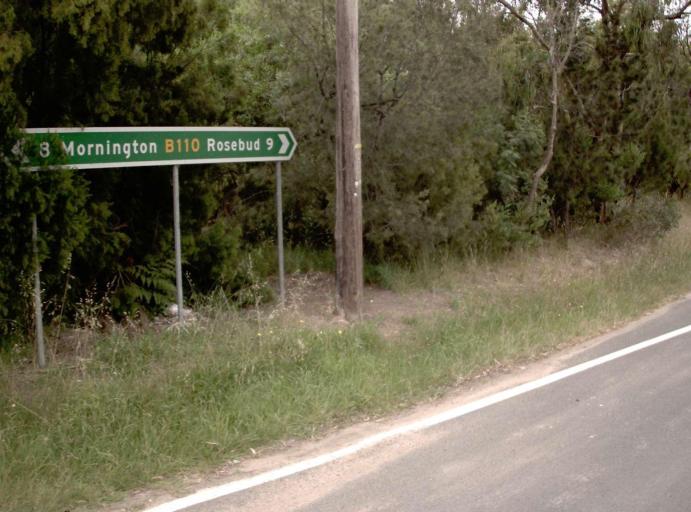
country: AU
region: Victoria
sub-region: Mornington Peninsula
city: Mount Martha
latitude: -38.2858
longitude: 145.0309
